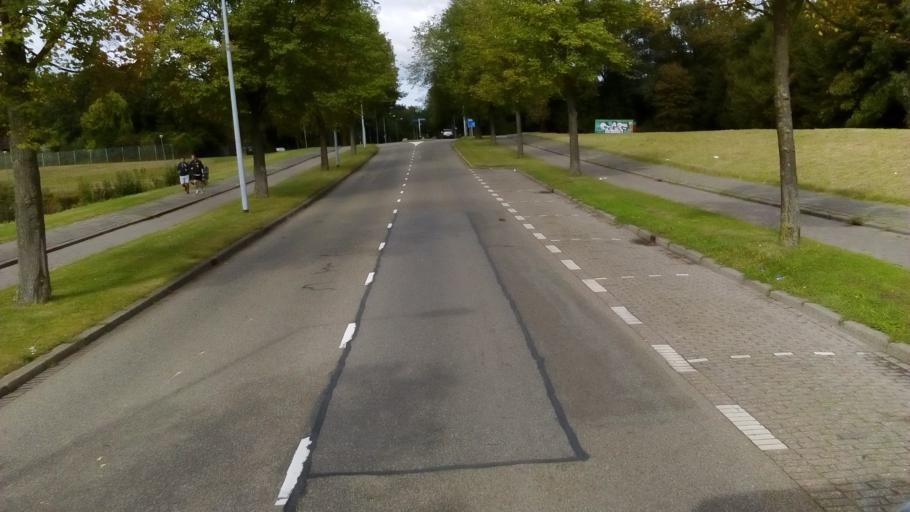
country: NL
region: South Holland
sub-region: Gemeente Schiedam
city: Schiedam
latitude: 51.9046
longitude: 4.3977
